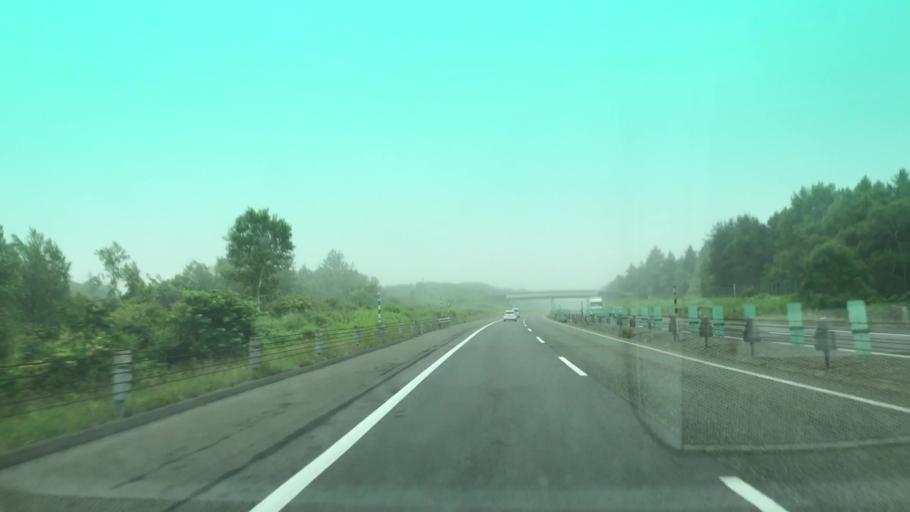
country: JP
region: Hokkaido
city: Chitose
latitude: 42.8291
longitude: 141.6132
